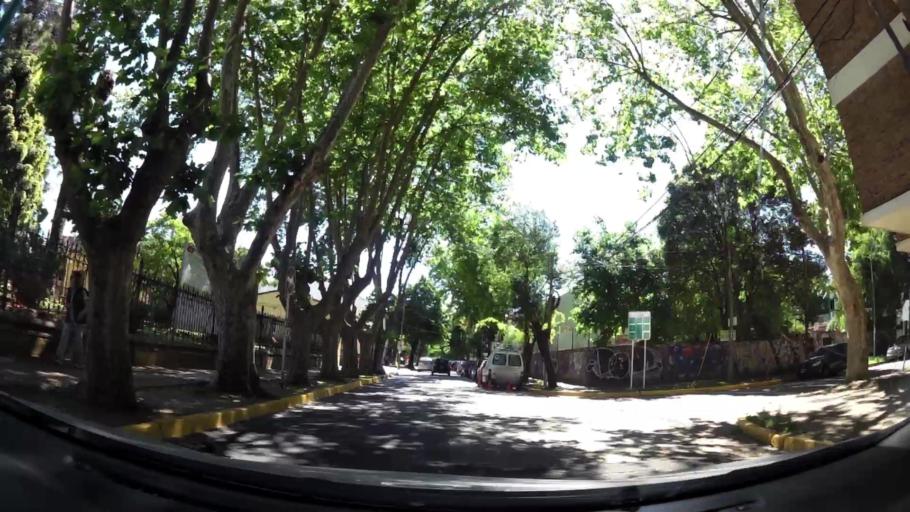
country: AR
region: Buenos Aires
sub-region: Partido de Vicente Lopez
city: Olivos
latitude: -34.5291
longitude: -58.4794
